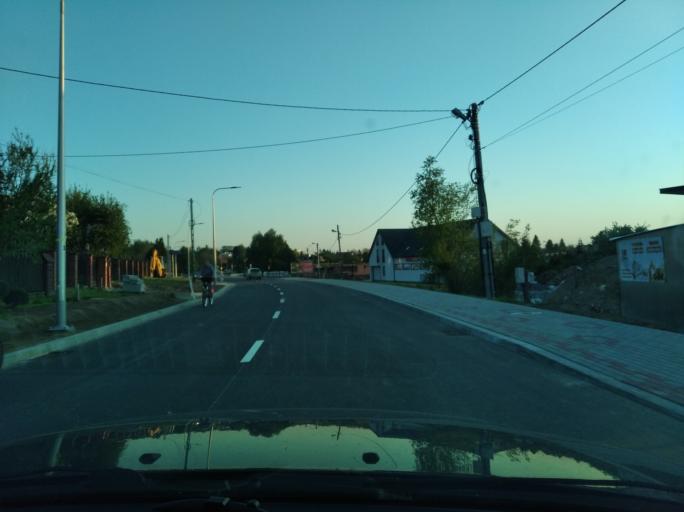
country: PL
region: Subcarpathian Voivodeship
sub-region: Powiat rzeszowski
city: Tyczyn
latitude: 50.0111
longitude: 22.0374
